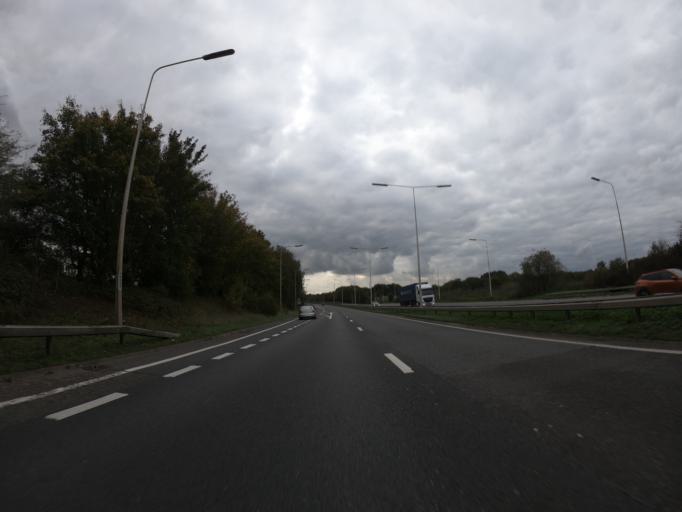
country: GB
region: England
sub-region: Borough of Thurrock
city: Chadwell St Mary
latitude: 51.4804
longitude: 0.3534
